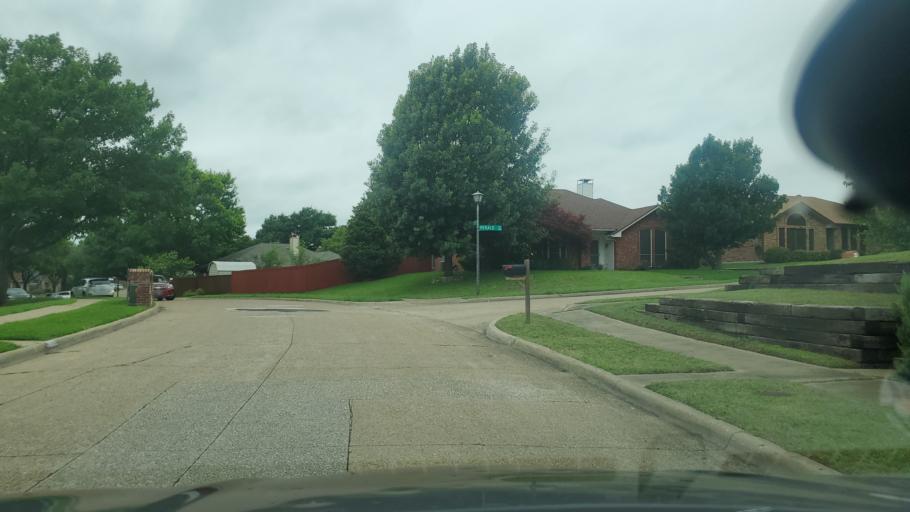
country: US
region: Texas
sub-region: Dallas County
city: Garland
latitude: 32.9545
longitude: -96.6620
